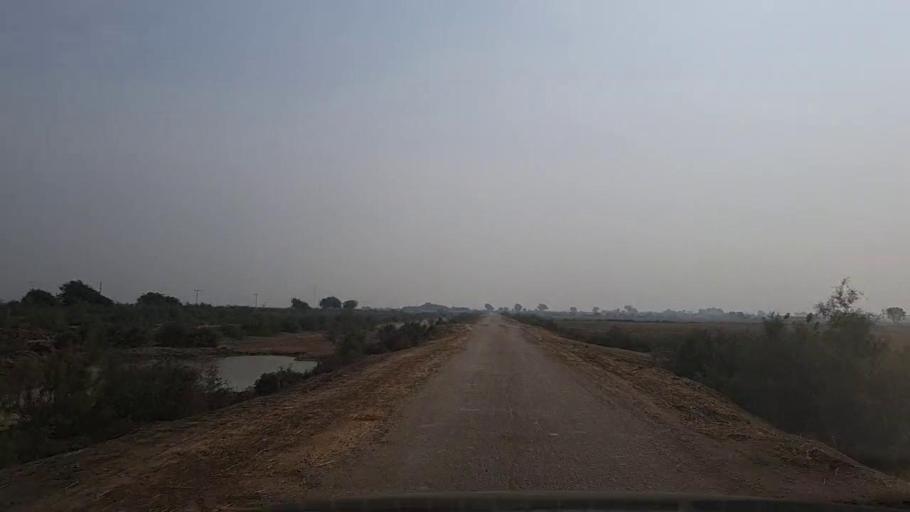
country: PK
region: Sindh
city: Mirpur Sakro
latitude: 24.3825
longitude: 67.7534
